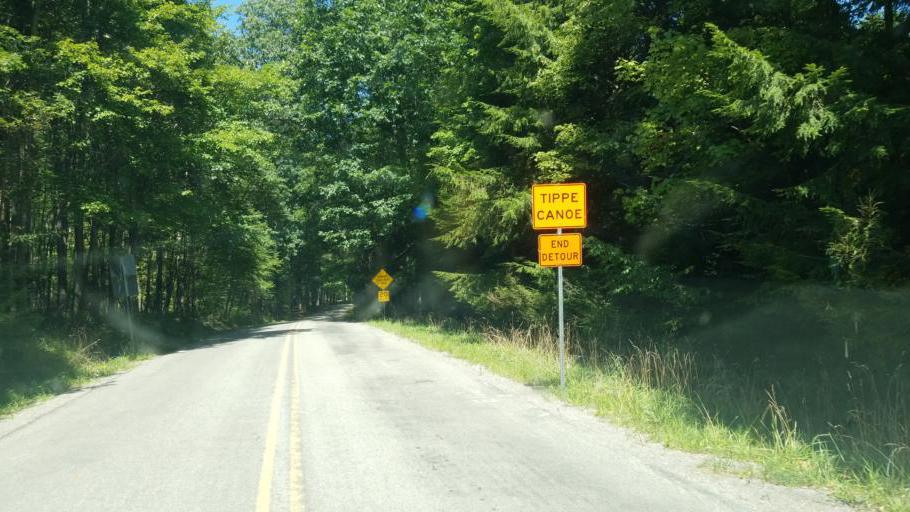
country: US
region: Pennsylvania
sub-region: Clarion County
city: Knox
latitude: 41.1797
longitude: -79.4838
